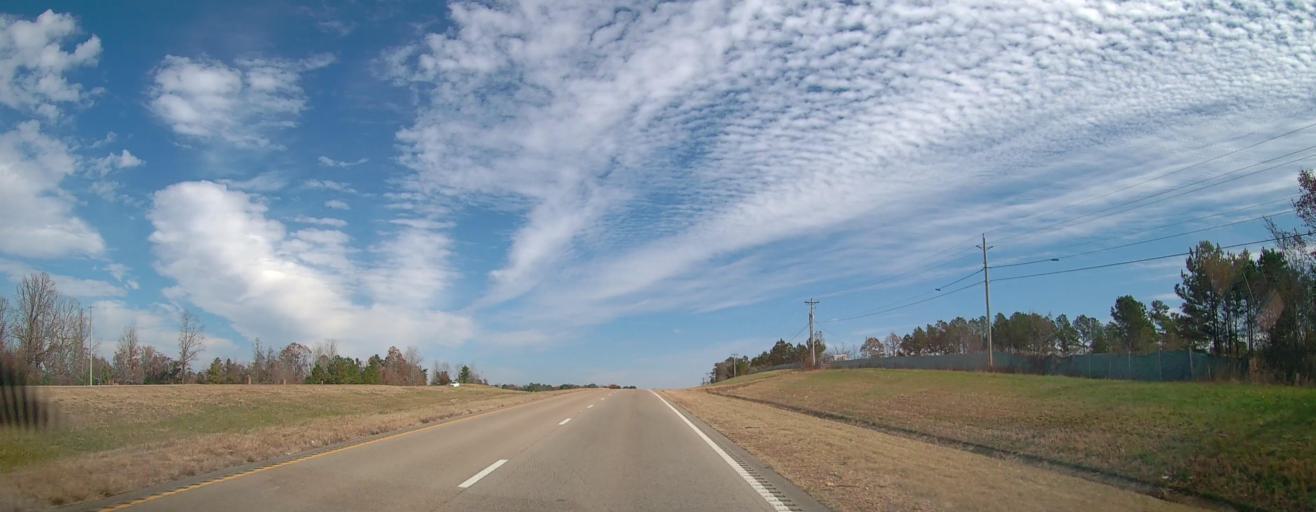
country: US
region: Mississippi
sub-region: Benton County
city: Ashland
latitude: 34.9545
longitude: -88.9936
